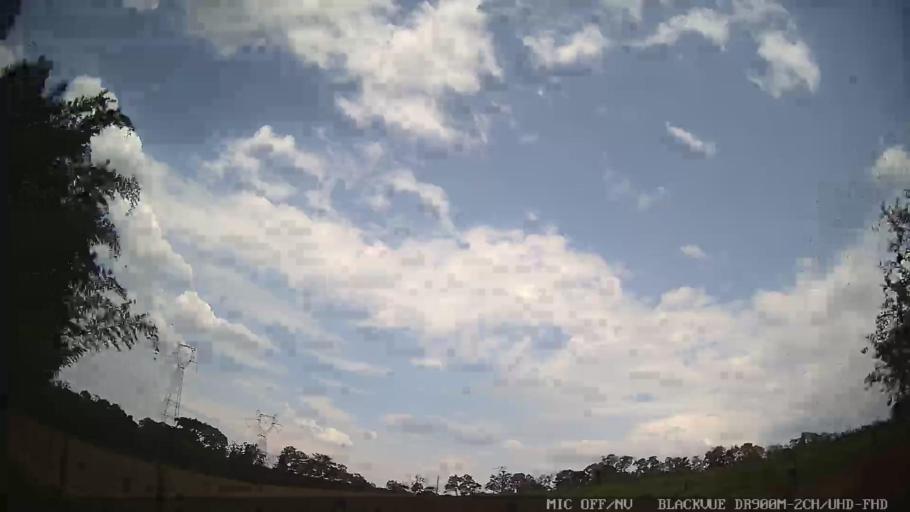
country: BR
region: Sao Paulo
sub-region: Louveira
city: Louveira
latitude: -23.1237
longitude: -46.9639
